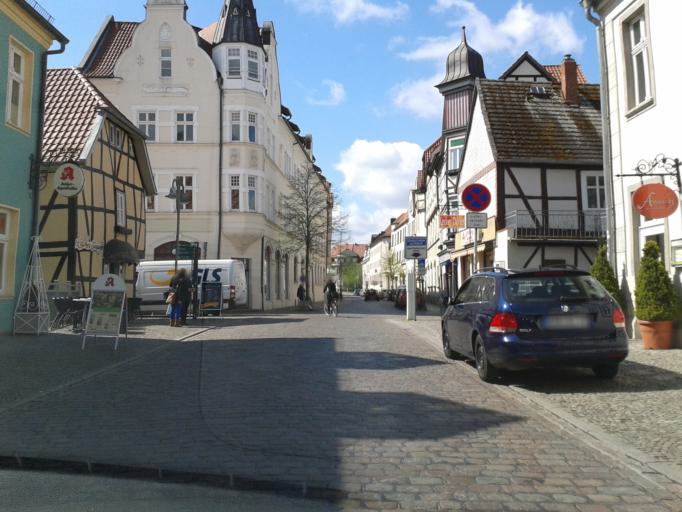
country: DE
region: Saxony-Anhalt
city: Salzwedel
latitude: 52.8529
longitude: 11.1533
